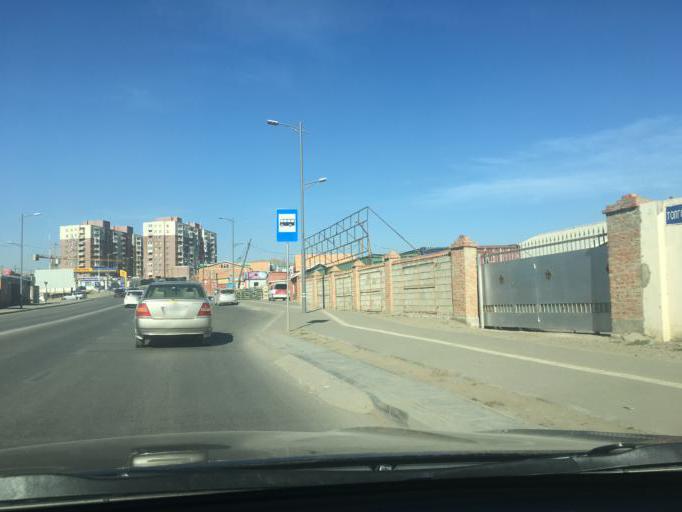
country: MN
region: Ulaanbaatar
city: Ulaanbaatar
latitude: 47.9132
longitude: 106.7824
